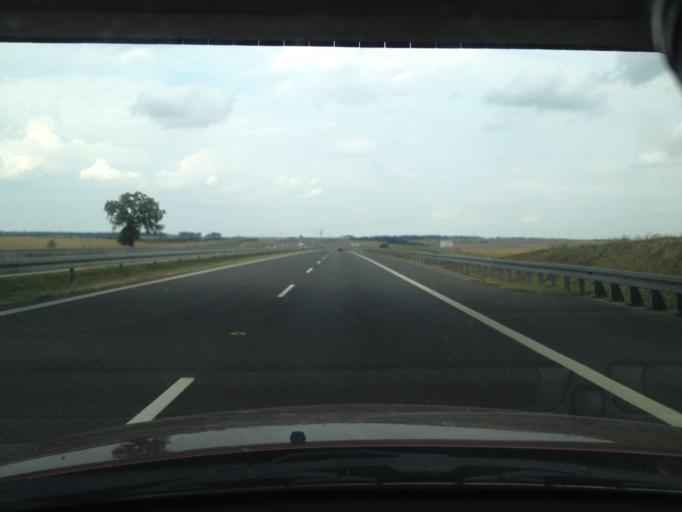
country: PL
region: West Pomeranian Voivodeship
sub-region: Powiat pyrzycki
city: Kozielice
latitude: 53.0307
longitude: 14.8637
